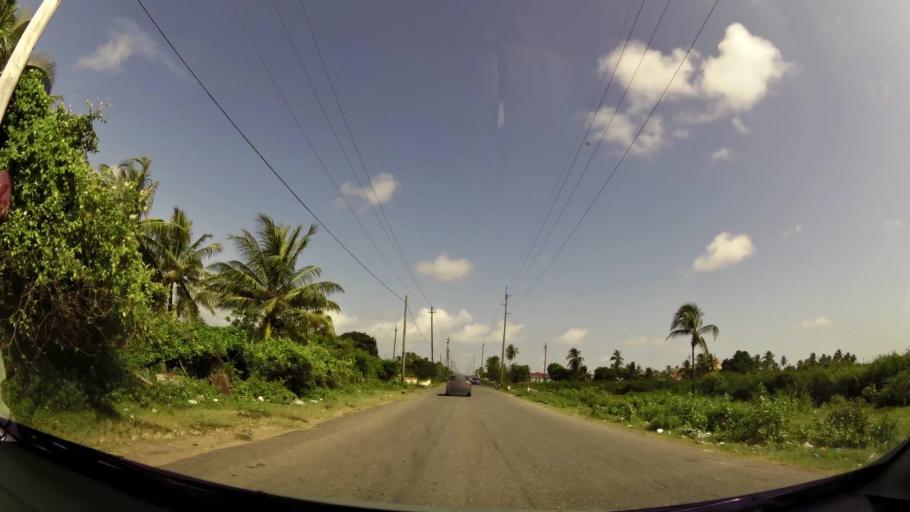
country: GY
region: Demerara-Mahaica
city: Mahaica Village
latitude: 6.7598
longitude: -57.9892
